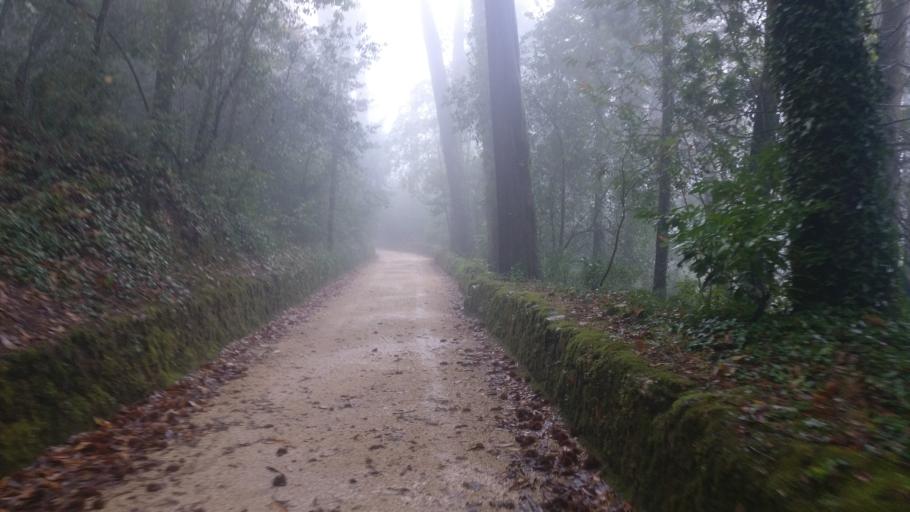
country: PT
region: Aveiro
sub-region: Mealhada
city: Pampilhosa do Botao
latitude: 40.3750
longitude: -8.3683
